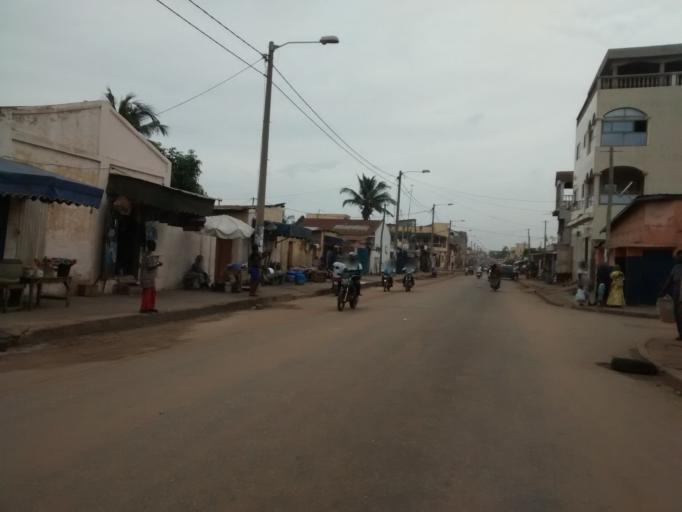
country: TG
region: Maritime
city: Lome
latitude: 6.1439
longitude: 1.2167
